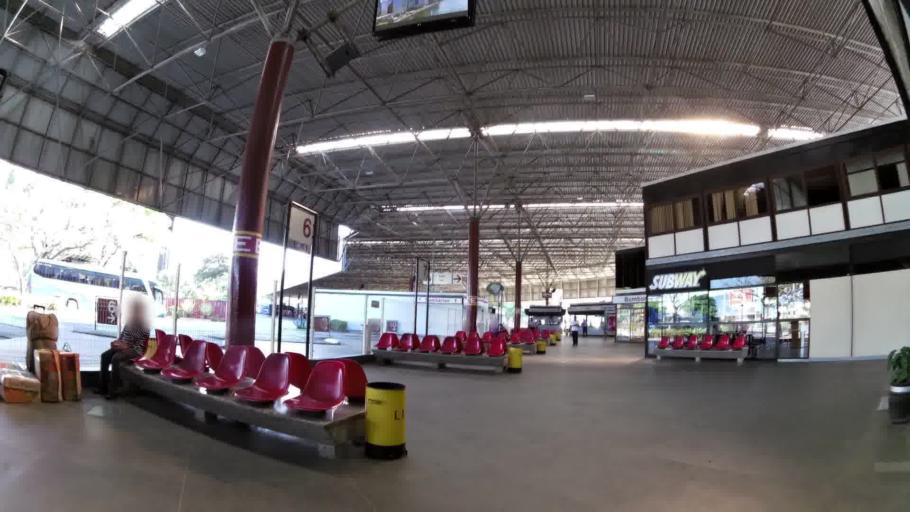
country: BR
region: Espirito Santo
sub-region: Vitoria
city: Vitoria
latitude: -20.3229
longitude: -40.3519
